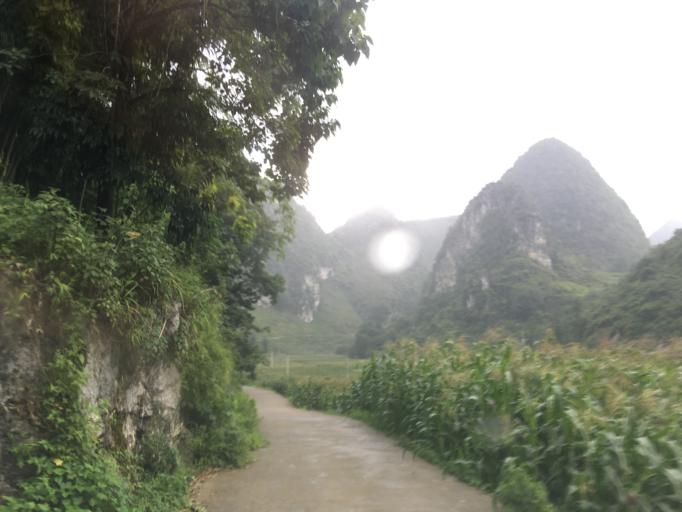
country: CN
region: Guangxi Zhuangzu Zizhiqu
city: Xinzhou
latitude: 24.9906
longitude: 105.6401
